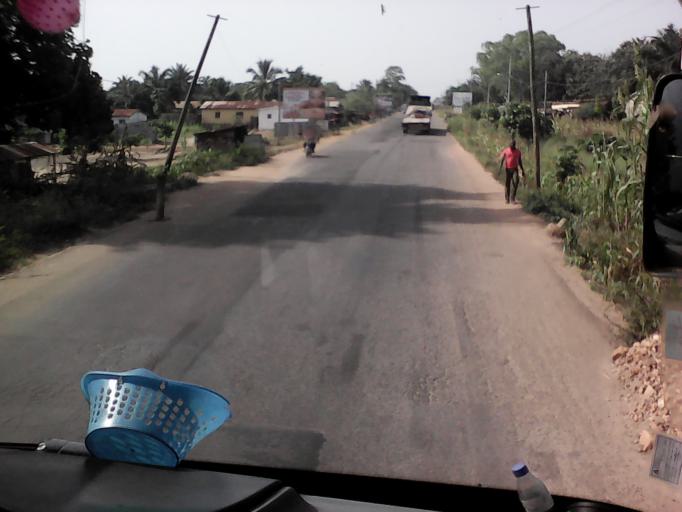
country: TG
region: Centrale
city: Sokode
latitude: 9.0130
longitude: 1.1378
